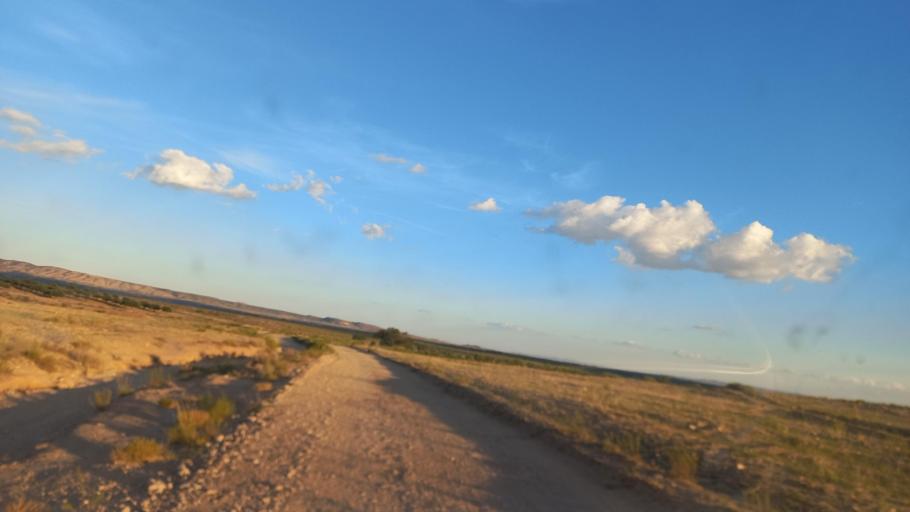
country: TN
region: Al Qasrayn
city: Sbiba
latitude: 35.3489
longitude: 9.0246
